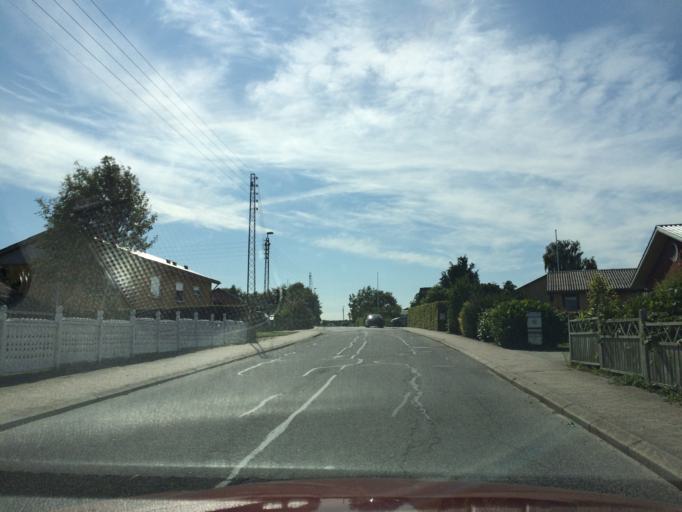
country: DK
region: Central Jutland
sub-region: Silkeborg Kommune
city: Svejbaek
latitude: 56.2254
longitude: 9.6283
